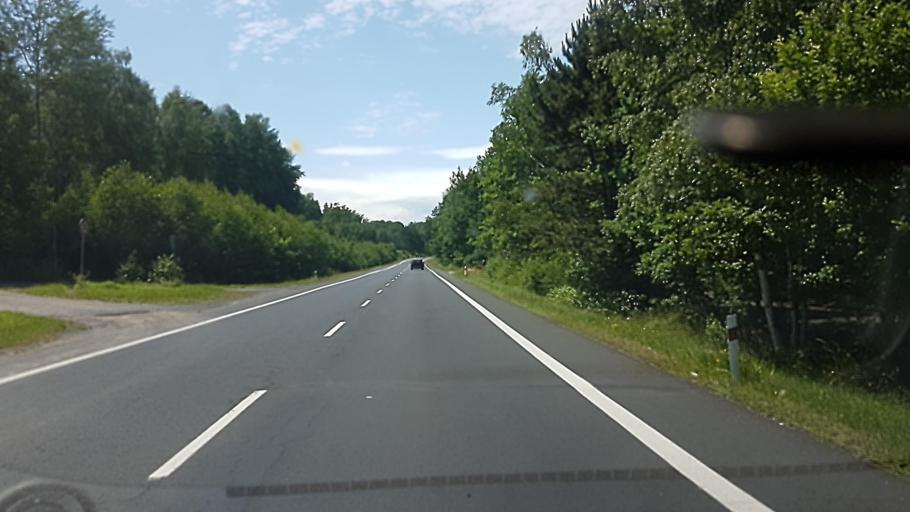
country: CZ
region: Karlovarsky
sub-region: Okres Cheb
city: Frantiskovy Lazne
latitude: 50.0814
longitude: 12.3195
